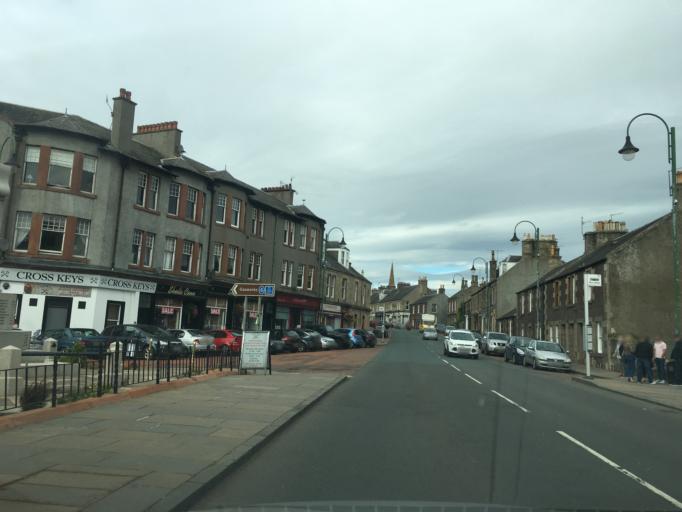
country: GB
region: Scotland
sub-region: South Lanarkshire
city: Biggar
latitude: 55.6223
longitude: -3.5280
